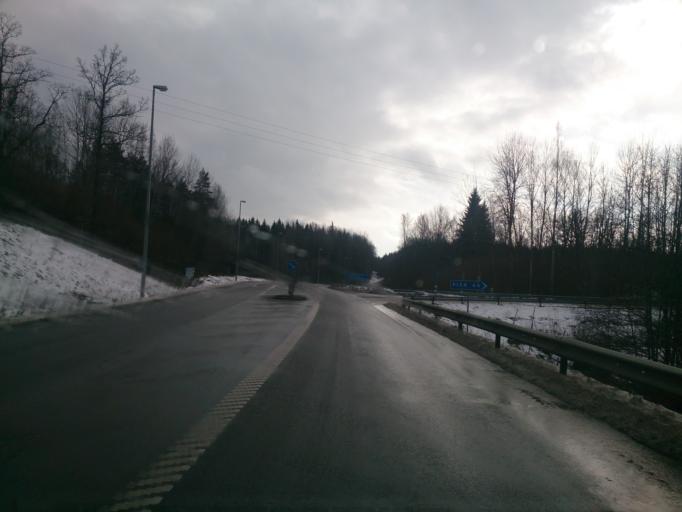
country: SE
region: OEstergoetland
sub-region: Atvidabergs Kommun
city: Atvidaberg
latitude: 58.1848
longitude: 16.0234
